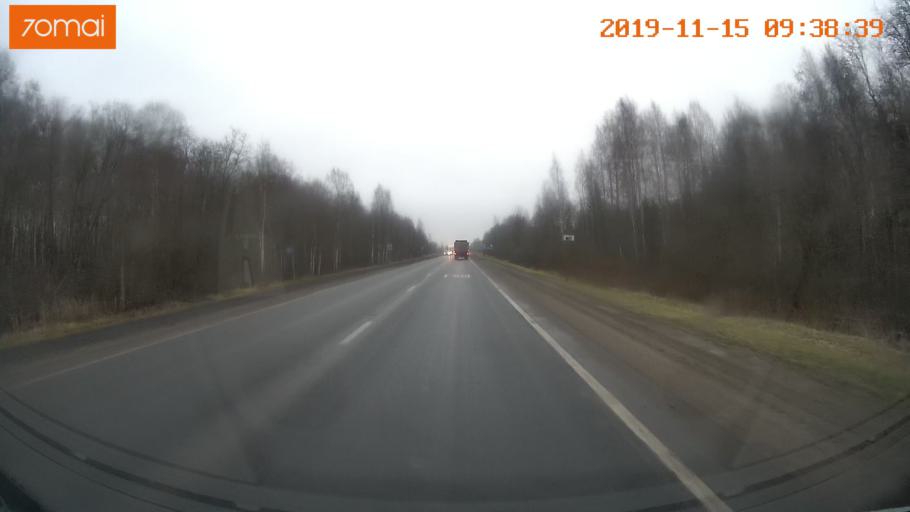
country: RU
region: Vologda
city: Sheksna
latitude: 59.2299
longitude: 38.4598
